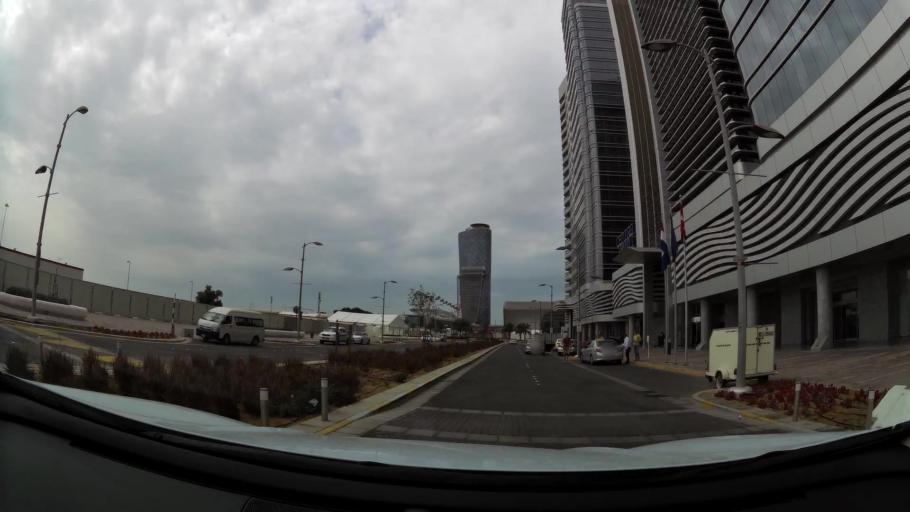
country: AE
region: Abu Dhabi
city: Abu Dhabi
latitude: 24.4175
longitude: 54.4410
